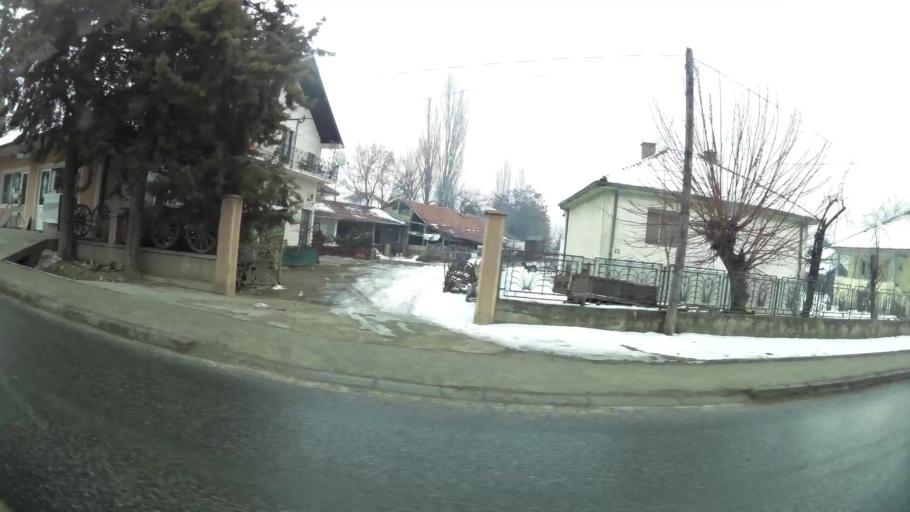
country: MK
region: Saraj
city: Saraj
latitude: 42.0274
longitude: 21.3530
